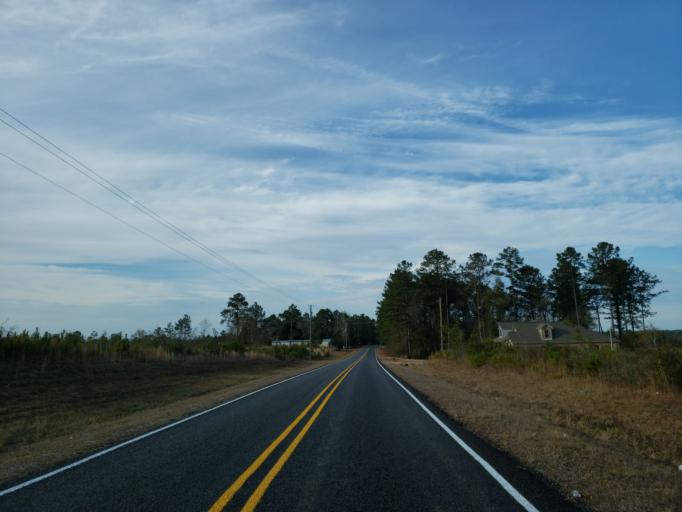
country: US
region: Mississippi
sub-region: Wayne County
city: Belmont
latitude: 31.4924
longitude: -88.5045
